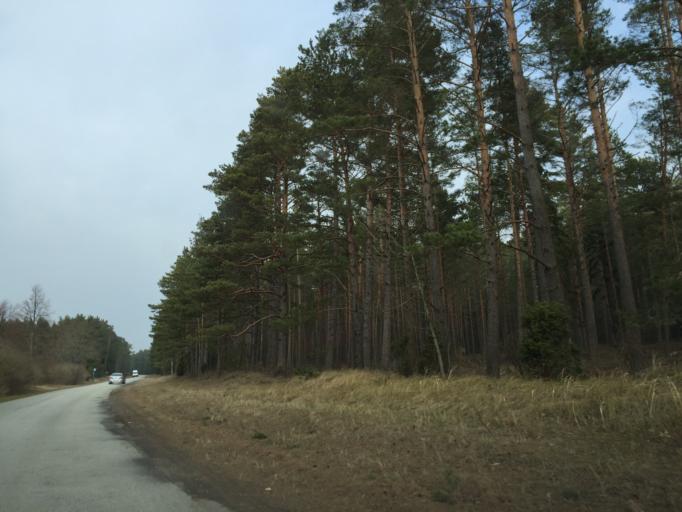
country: LV
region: Salacgrivas
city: Ainazi
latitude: 57.9347
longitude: 24.3917
